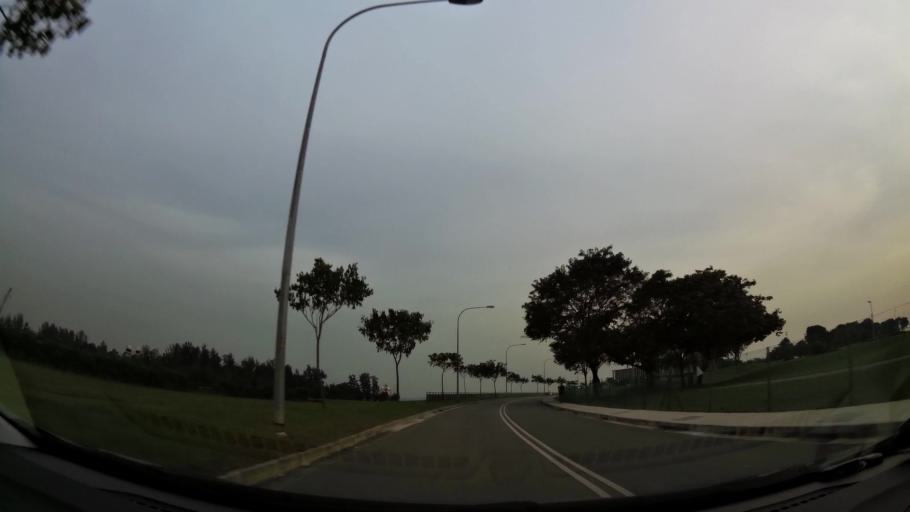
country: SG
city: Singapore
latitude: 1.2866
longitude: 103.8776
